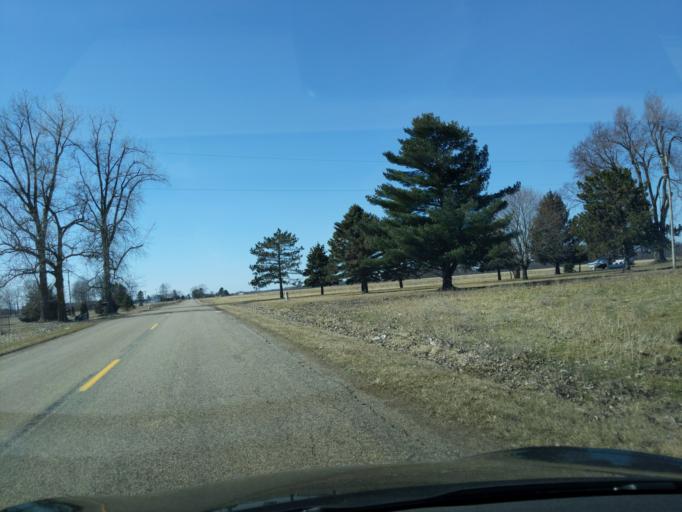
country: US
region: Michigan
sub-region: Ionia County
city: Portland
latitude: 42.7266
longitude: -84.9119
